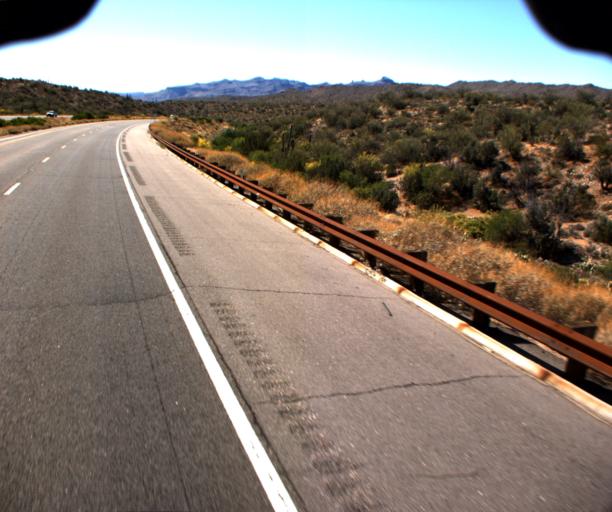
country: US
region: Arizona
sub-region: Yavapai County
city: Bagdad
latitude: 34.4178
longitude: -113.2348
